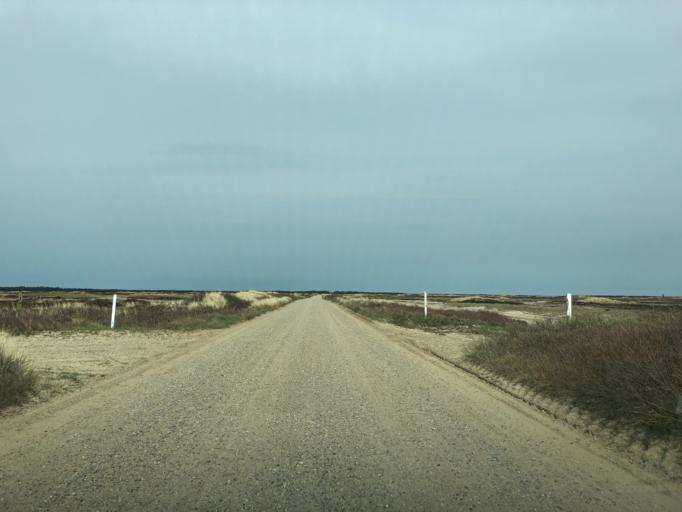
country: DK
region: South Denmark
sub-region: Varde Kommune
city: Oksbol
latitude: 55.5758
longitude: 8.1406
